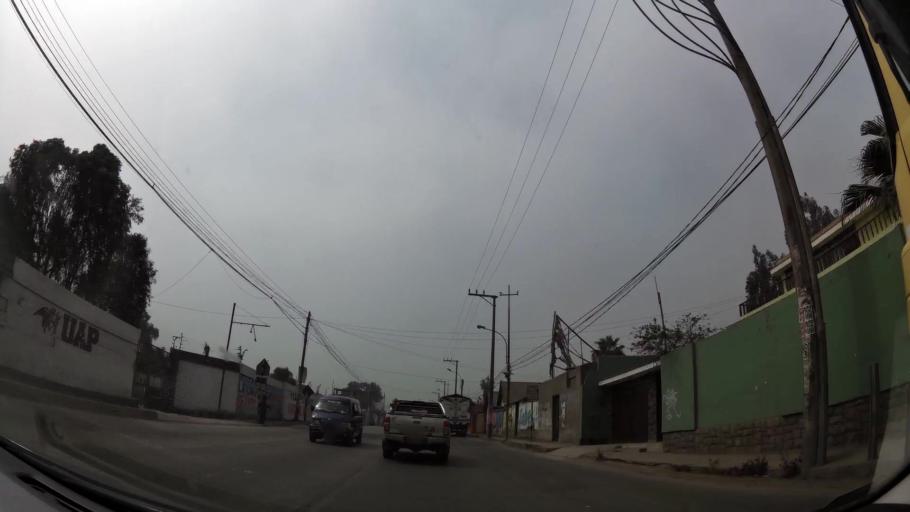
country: PE
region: Lima
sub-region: Lima
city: Chaclacayo
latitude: -11.9707
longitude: -76.7527
